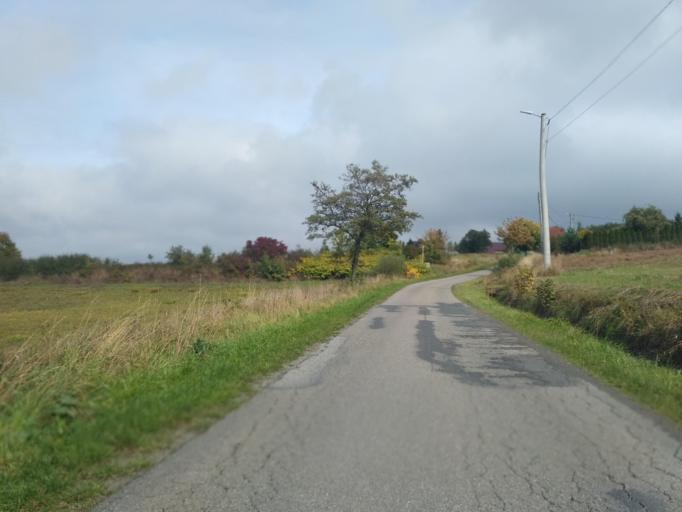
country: PL
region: Subcarpathian Voivodeship
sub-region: Powiat ropczycko-sedziszowski
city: Niedzwiada
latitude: 49.9618
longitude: 21.4428
